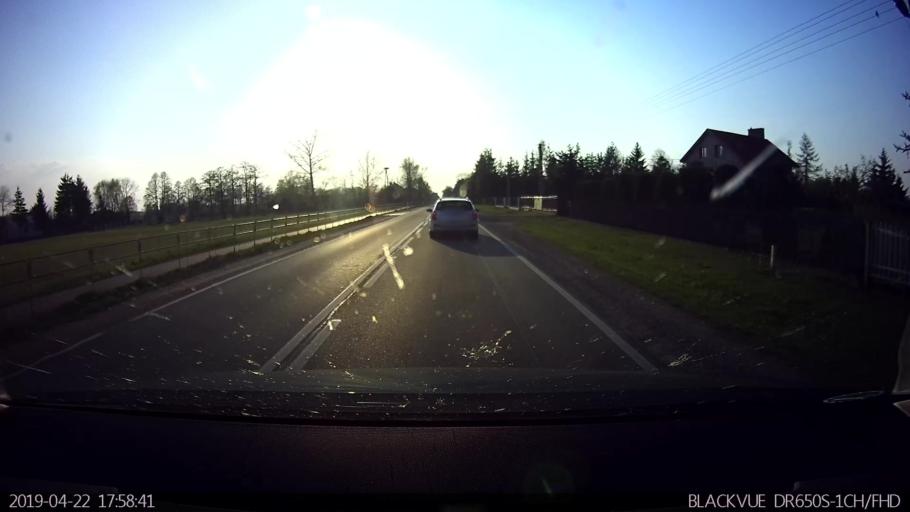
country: PL
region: Masovian Voivodeship
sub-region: Powiat wegrowski
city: Korytnica
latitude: 52.4724
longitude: 21.8734
